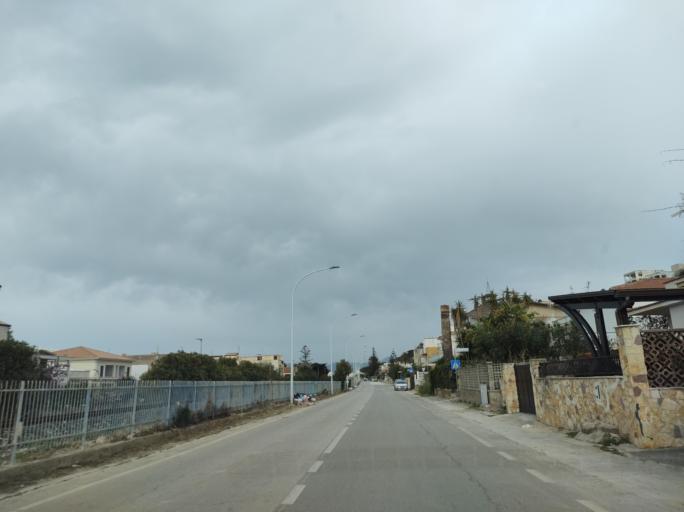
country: IT
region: Sicily
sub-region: Trapani
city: Alcamo
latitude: 38.0263
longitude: 12.9290
